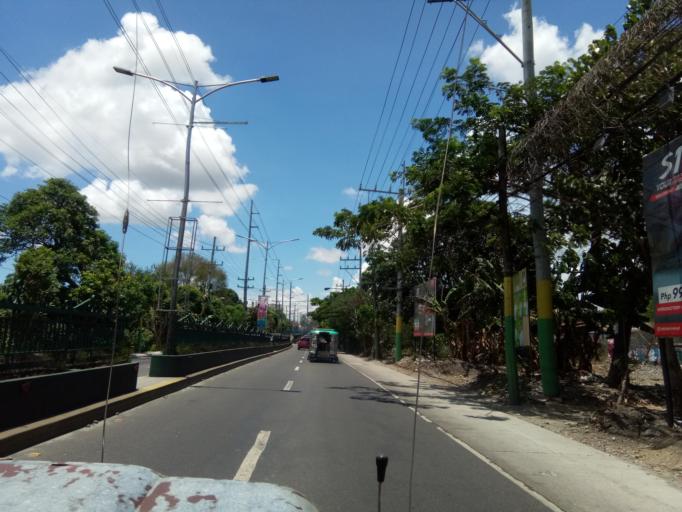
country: PH
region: Calabarzon
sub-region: Province of Cavite
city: Dasmarinas
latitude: 14.3099
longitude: 120.9502
